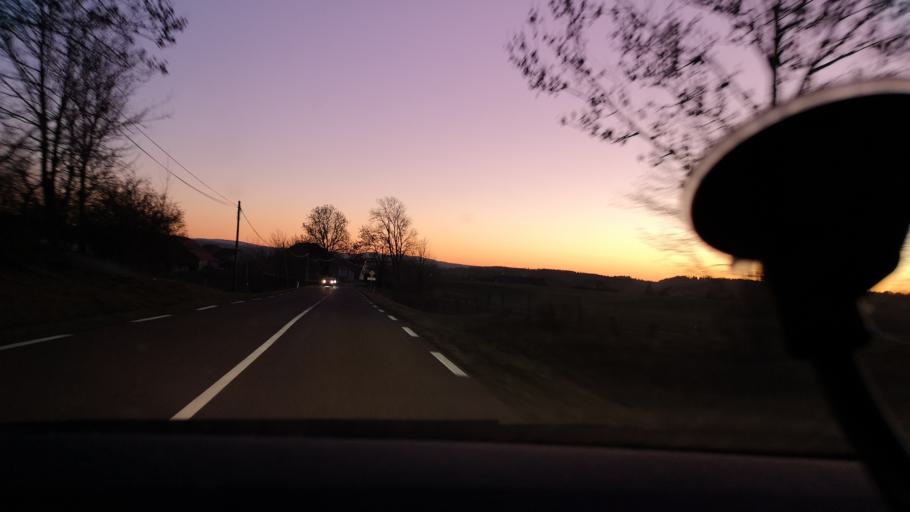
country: FR
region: Franche-Comte
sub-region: Departement du Jura
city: Champagnole
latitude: 46.7839
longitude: 6.0055
